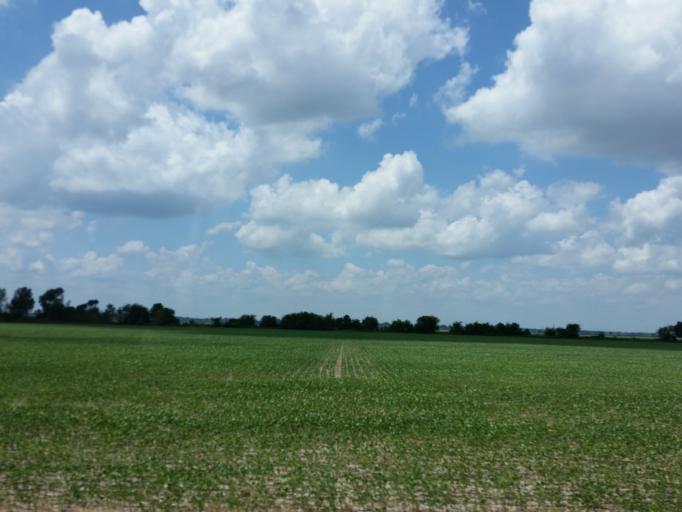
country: US
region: Tennessee
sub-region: Lake County
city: Ridgely
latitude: 36.2800
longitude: -89.4770
